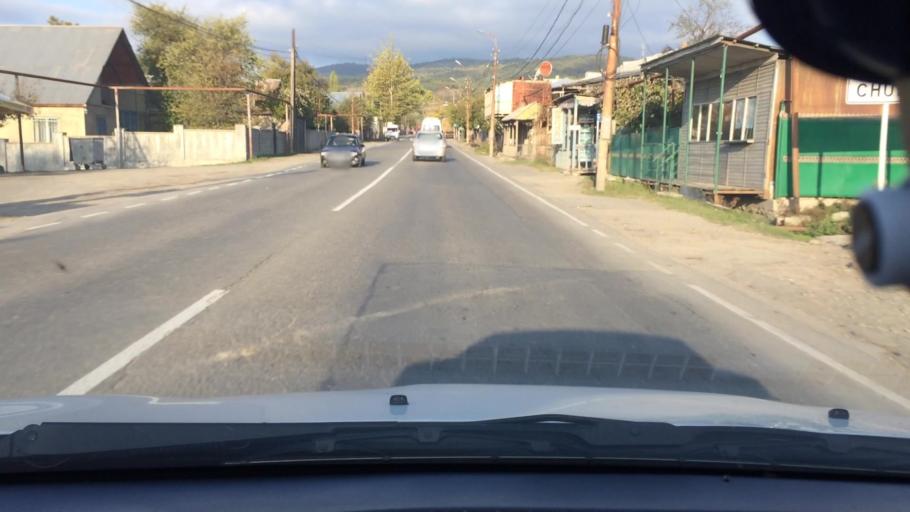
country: GE
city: Surami
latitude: 42.0282
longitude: 43.5355
